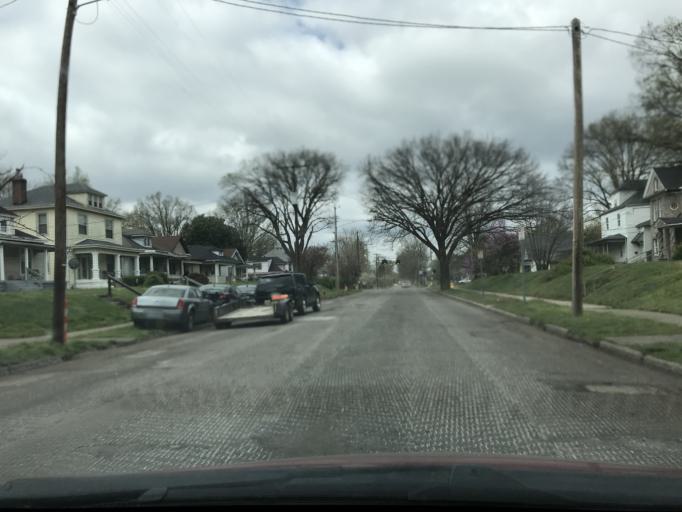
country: US
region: Kentucky
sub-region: Jefferson County
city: Shively
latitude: 38.2387
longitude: -85.8057
